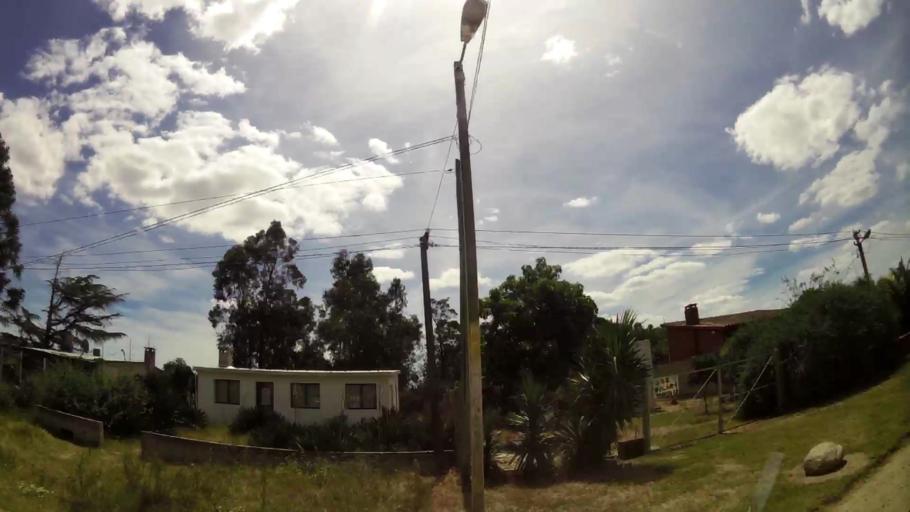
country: UY
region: San Jose
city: Delta del Tigre
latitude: -34.7495
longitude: -56.4569
